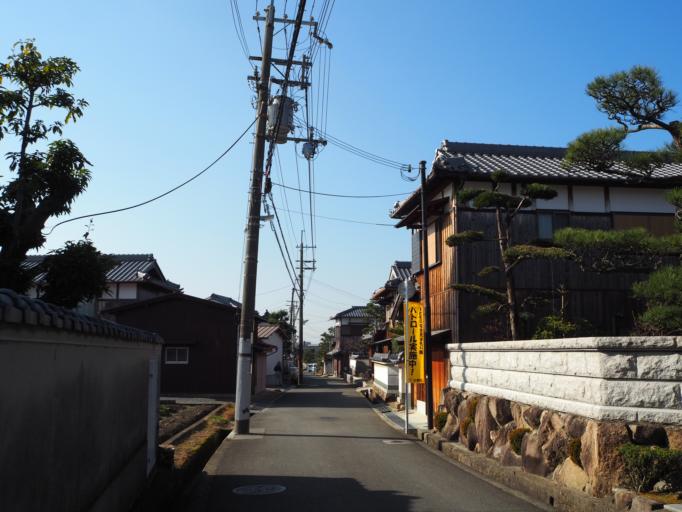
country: JP
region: Osaka
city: Mino
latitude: 34.8274
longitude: 135.4826
